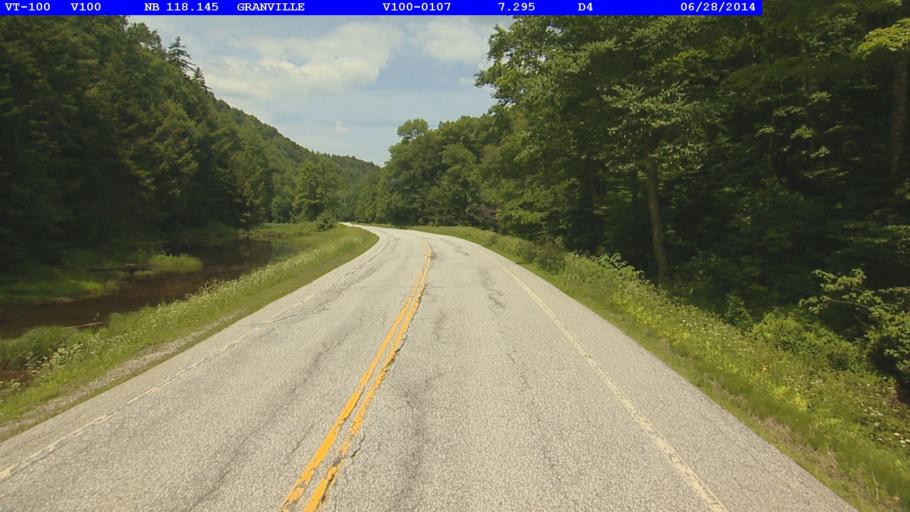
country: US
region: Vermont
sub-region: Orange County
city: Randolph
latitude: 44.0355
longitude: -72.8315
